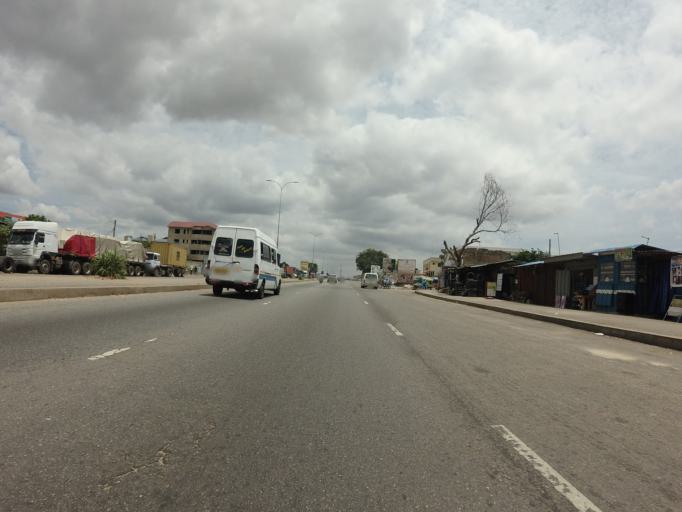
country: GH
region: Greater Accra
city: Gbawe
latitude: 5.5789
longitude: -0.2679
